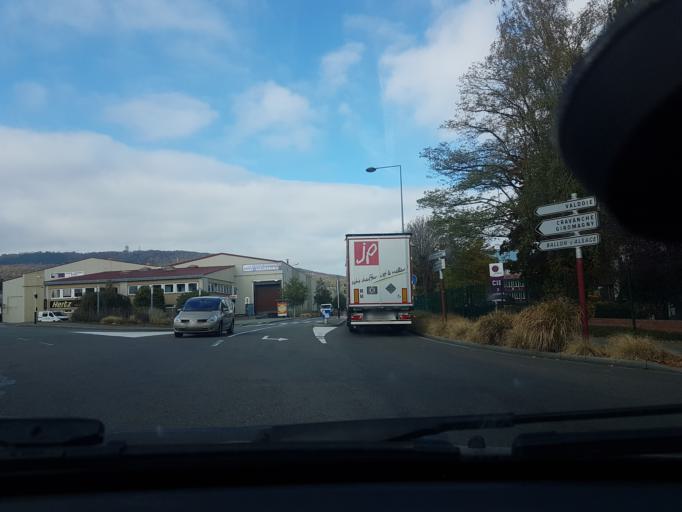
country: FR
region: Franche-Comte
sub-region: Territoire de Belfort
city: Cravanche
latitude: 47.6470
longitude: 6.8396
